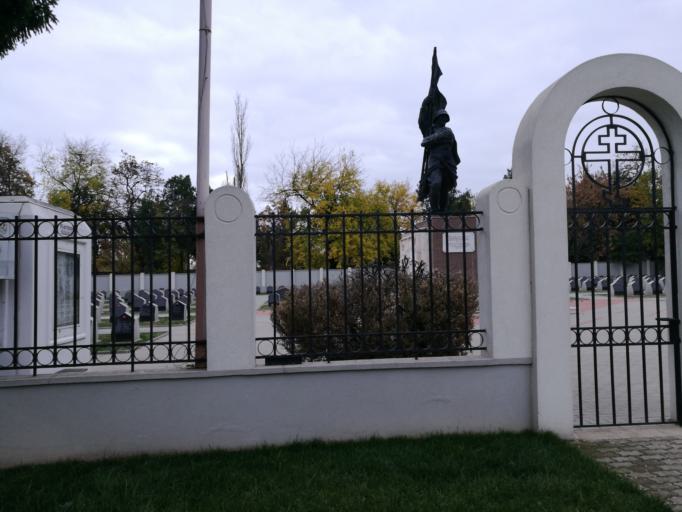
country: RO
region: Bucuresti
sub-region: Municipiul Bucuresti
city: Bucharest
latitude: 44.4788
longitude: 26.0974
